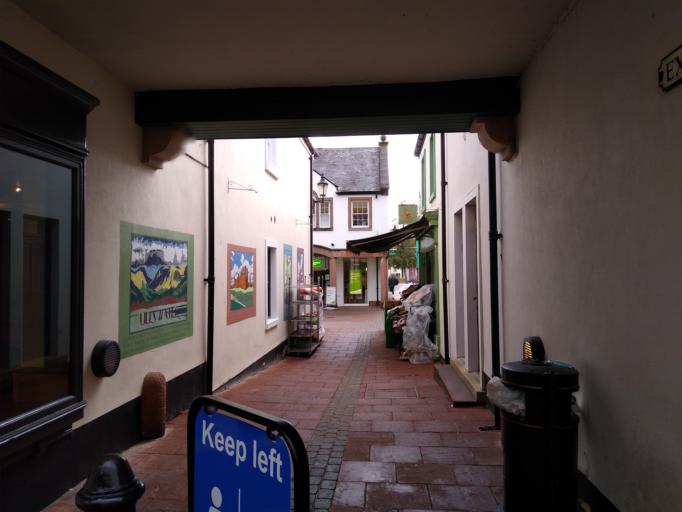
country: GB
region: England
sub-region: Cumbria
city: Penrith
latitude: 54.6634
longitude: -2.7525
